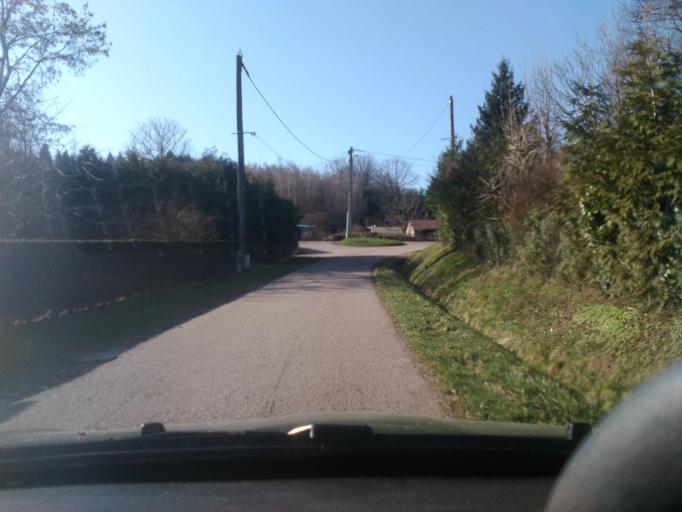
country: FR
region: Lorraine
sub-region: Departement des Vosges
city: Moyenmoutier
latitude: 48.3688
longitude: 6.8959
